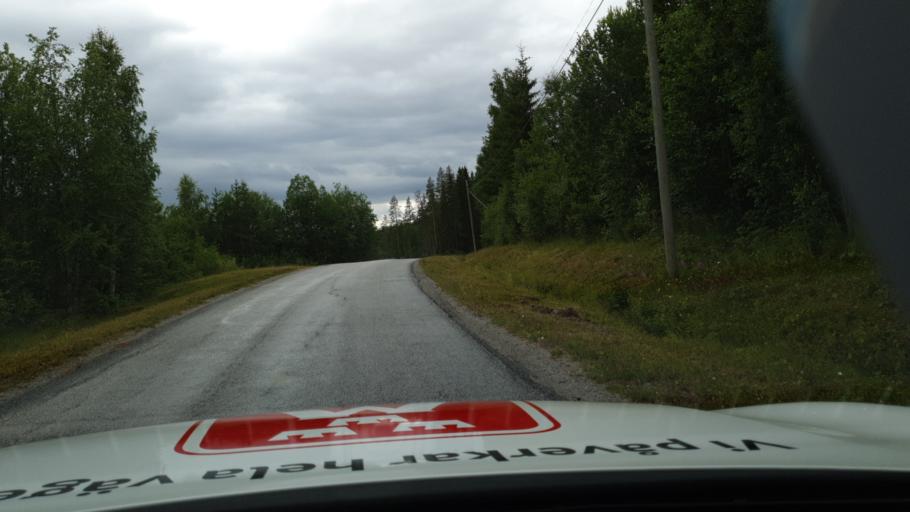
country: SE
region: Vaesterbotten
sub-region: Dorotea Kommun
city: Dorotea
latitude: 64.1296
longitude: 16.2475
